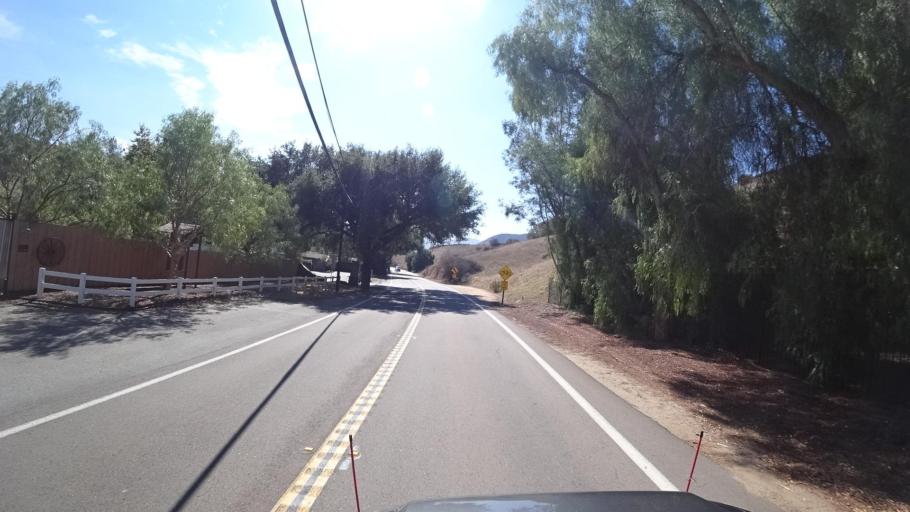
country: US
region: California
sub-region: San Diego County
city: Crest
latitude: 32.8015
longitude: -116.8450
